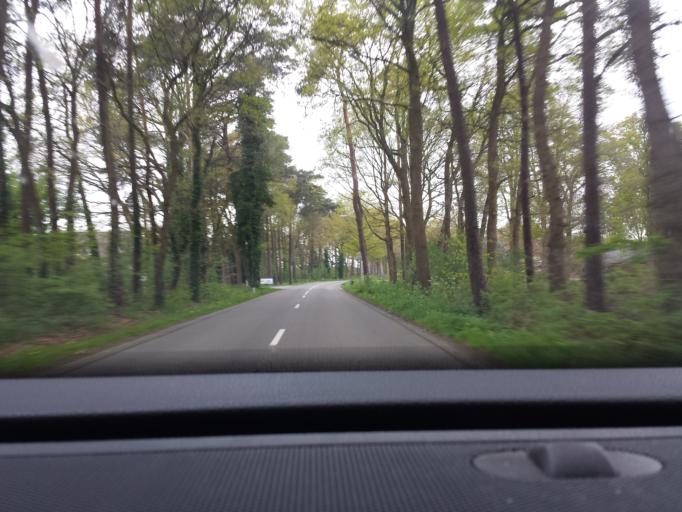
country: NL
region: Gelderland
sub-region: Gemeente Bronckhorst
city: Hengelo
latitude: 52.0603
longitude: 6.3435
